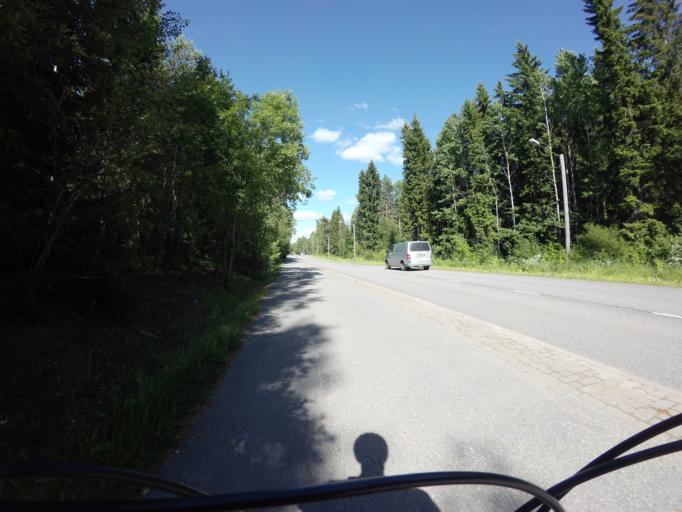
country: FI
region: Varsinais-Suomi
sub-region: Turku
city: Vahto
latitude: 60.5300
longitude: 22.2983
